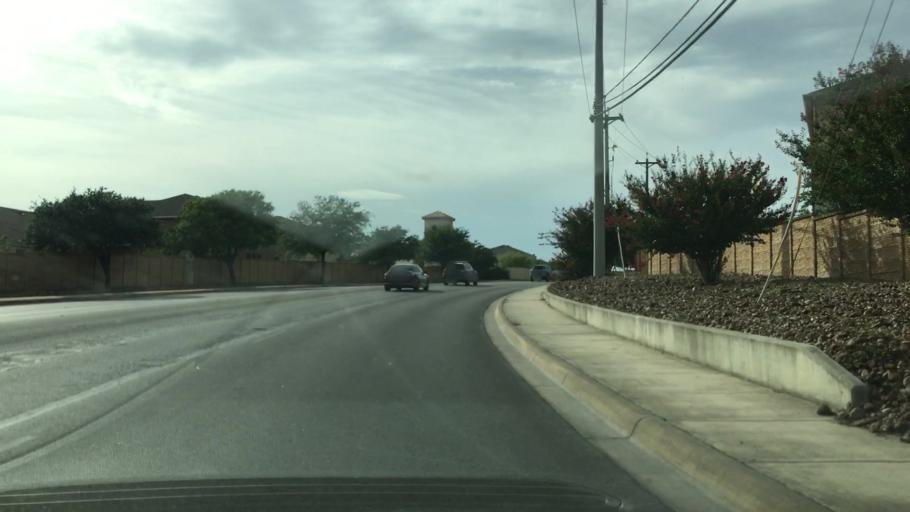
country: US
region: Texas
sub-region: Guadalupe County
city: Northcliff
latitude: 29.5983
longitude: -98.2587
